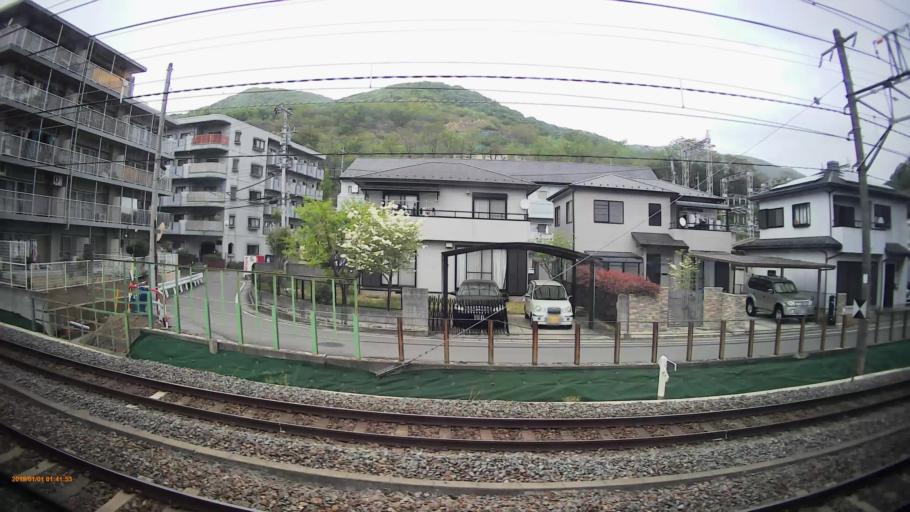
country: JP
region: Yamanashi
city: Isawa
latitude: 35.6588
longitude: 138.6017
